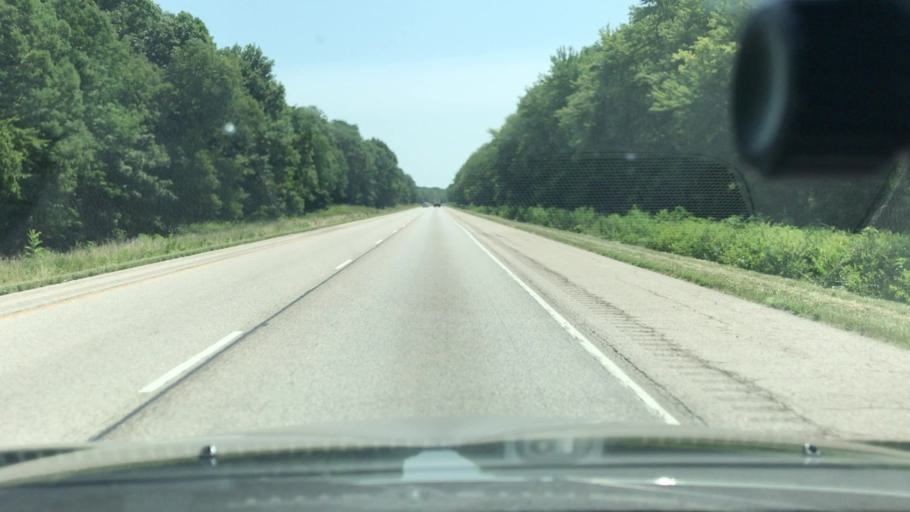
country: US
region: Illinois
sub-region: Washington County
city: Nashville
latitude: 38.4101
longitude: -89.4250
